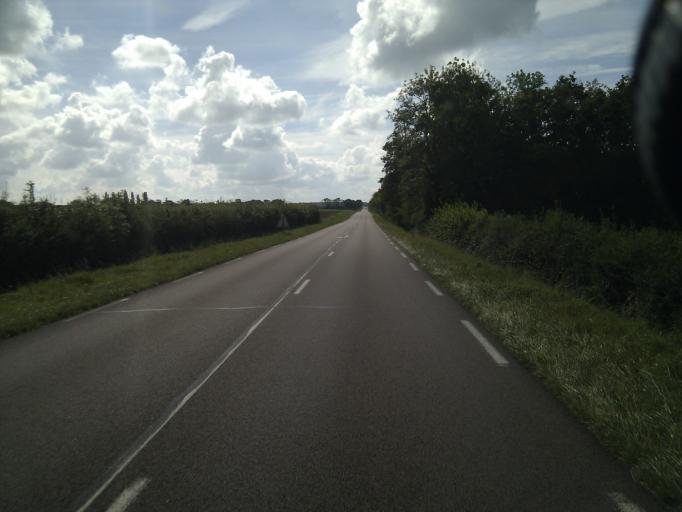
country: FR
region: Bourgogne
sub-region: Departement de la Cote-d'Or
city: Semur-en-Auxois
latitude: 47.4790
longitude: 4.3203
